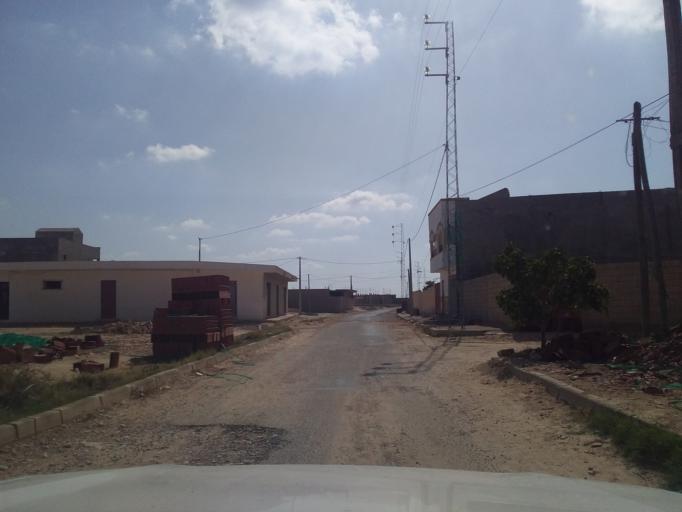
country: TN
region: Madanin
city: Medenine
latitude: 33.5828
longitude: 10.3263
